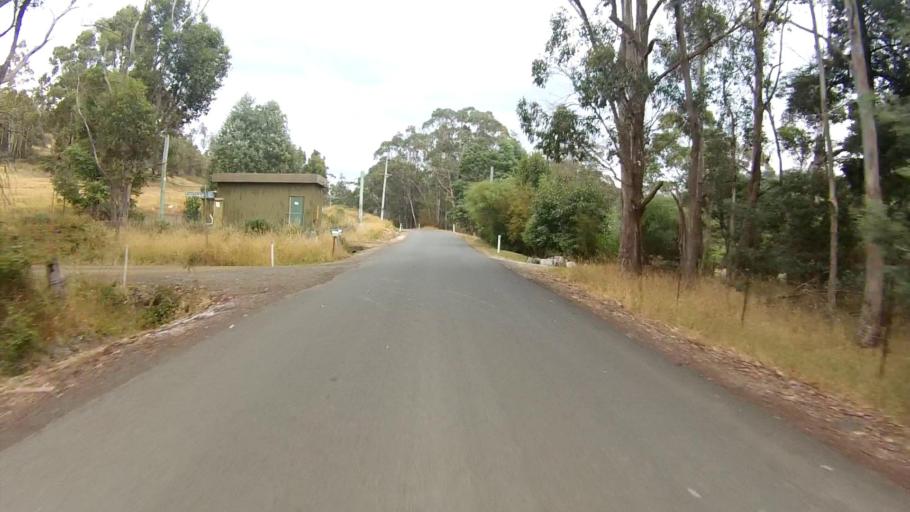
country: AU
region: Tasmania
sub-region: Huon Valley
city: Cygnet
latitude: -43.2399
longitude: 147.1527
